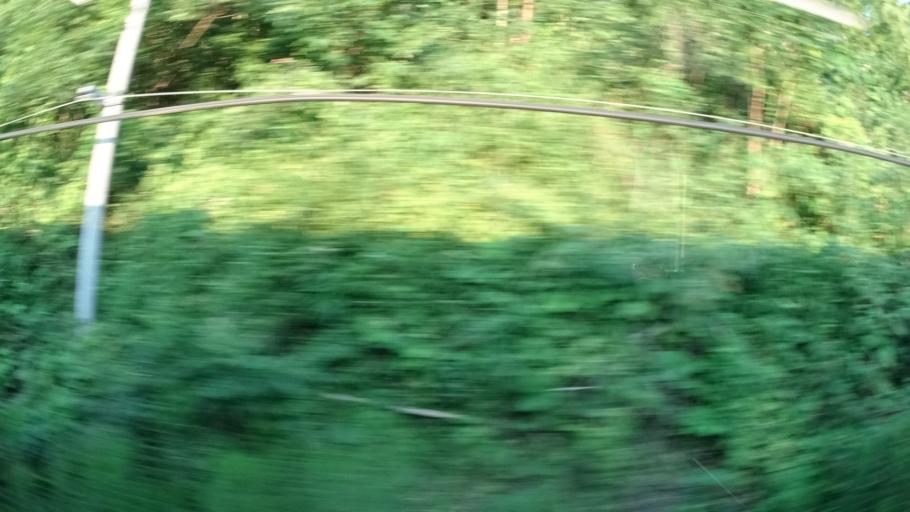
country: JP
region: Ibaraki
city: Naka
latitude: 36.0596
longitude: 140.1874
